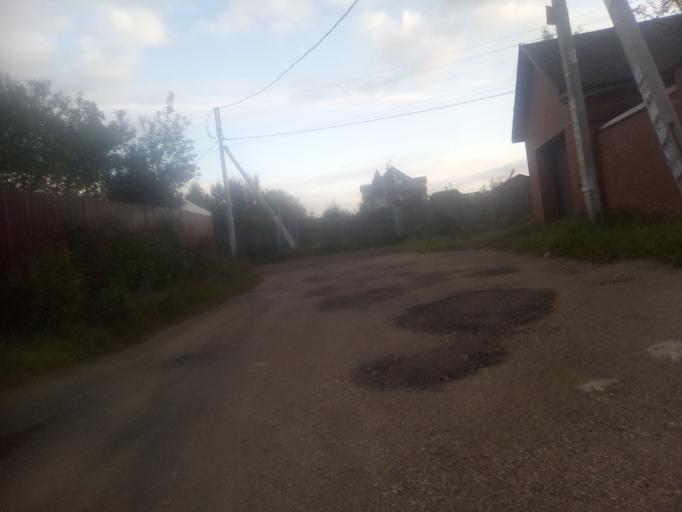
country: RU
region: Moskovskaya
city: Golitsyno
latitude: 55.5675
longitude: 37.0012
